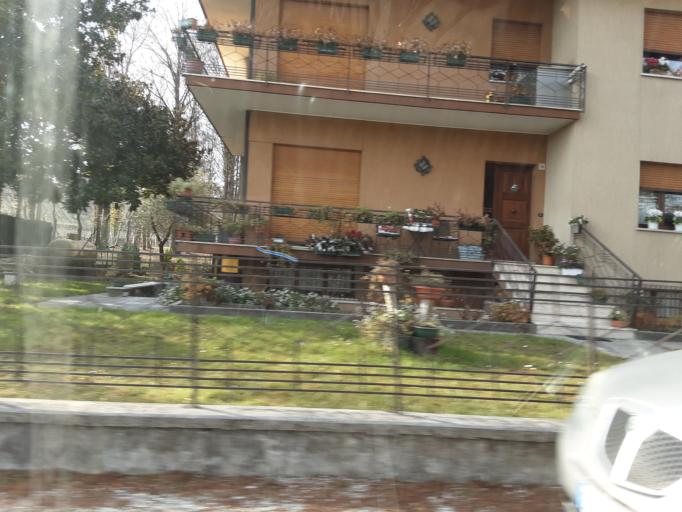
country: IT
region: Veneto
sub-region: Provincia di Treviso
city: Carpesica
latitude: 45.9611
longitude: 12.2842
